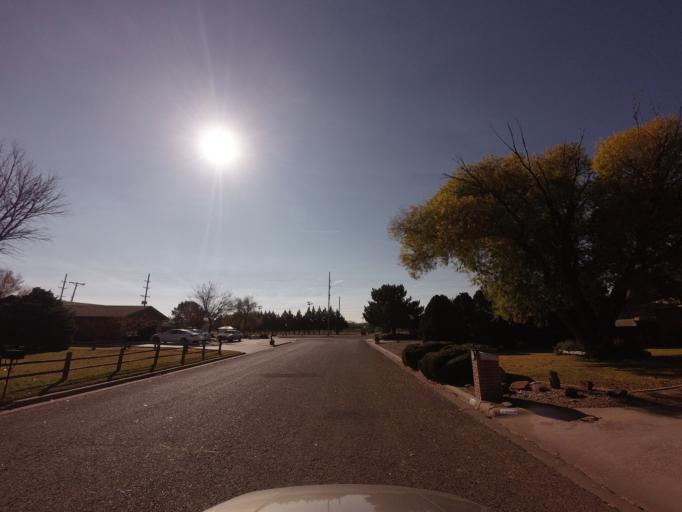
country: US
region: New Mexico
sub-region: Curry County
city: Clovis
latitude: 34.4126
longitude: -103.1821
